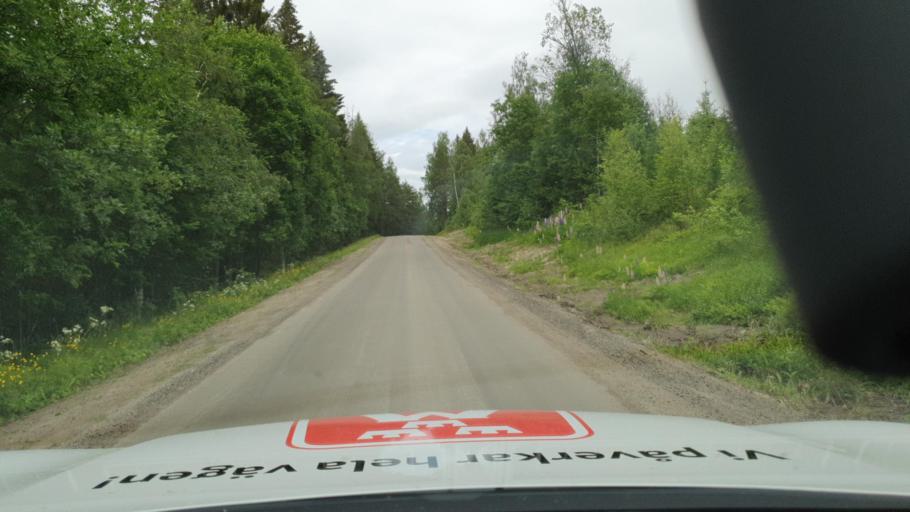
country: SE
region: Vaesterbotten
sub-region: Nordmalings Kommun
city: Nordmaling
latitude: 63.6787
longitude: 19.4440
